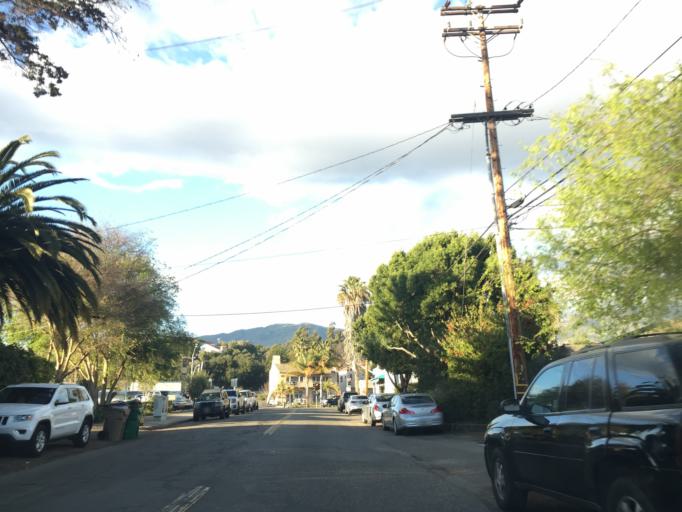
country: US
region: California
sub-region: Santa Barbara County
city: Goleta
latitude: 34.4390
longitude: -119.7711
